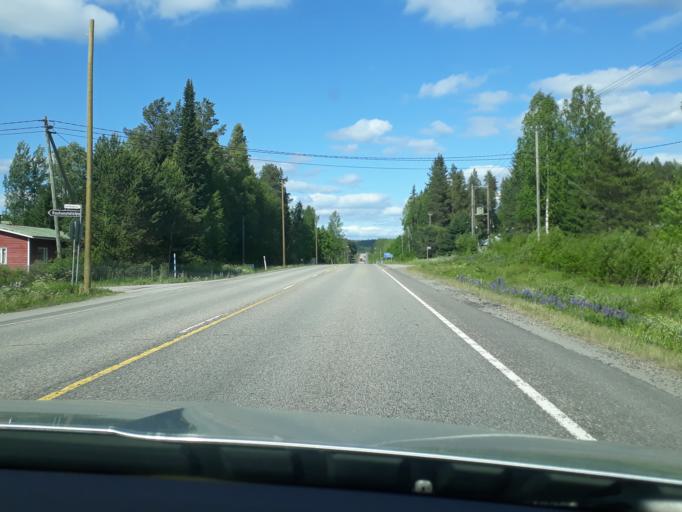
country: FI
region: Central Finland
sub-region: AEaenekoski
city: AEaenekoski
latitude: 62.6550
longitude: 25.7239
